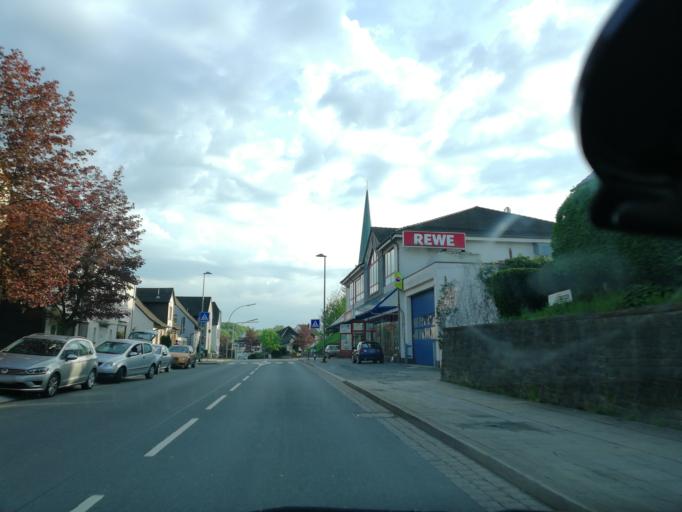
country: DE
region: North Rhine-Westphalia
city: Wetter (Ruhr)
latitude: 51.3746
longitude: 7.3706
